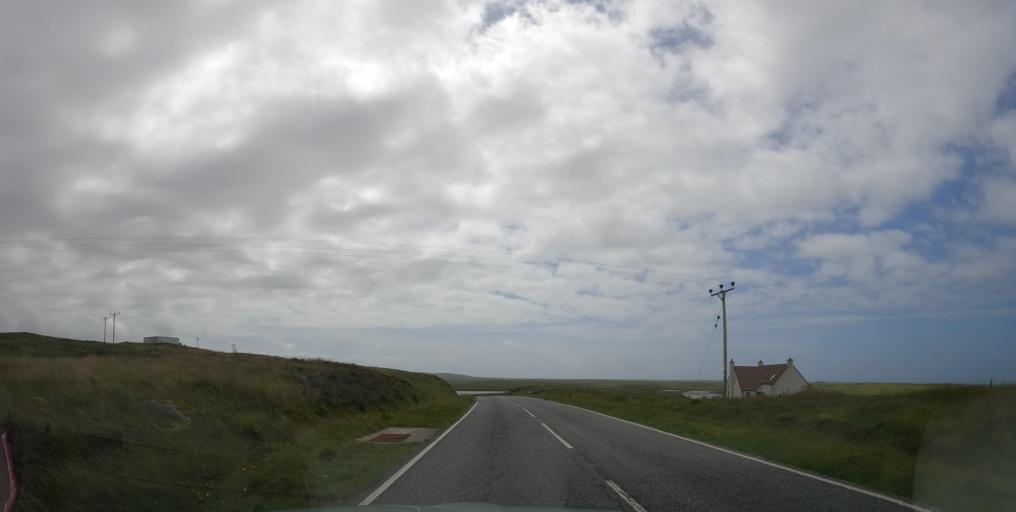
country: GB
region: Scotland
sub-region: Eilean Siar
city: Isle of South Uist
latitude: 57.2698
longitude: -7.3670
